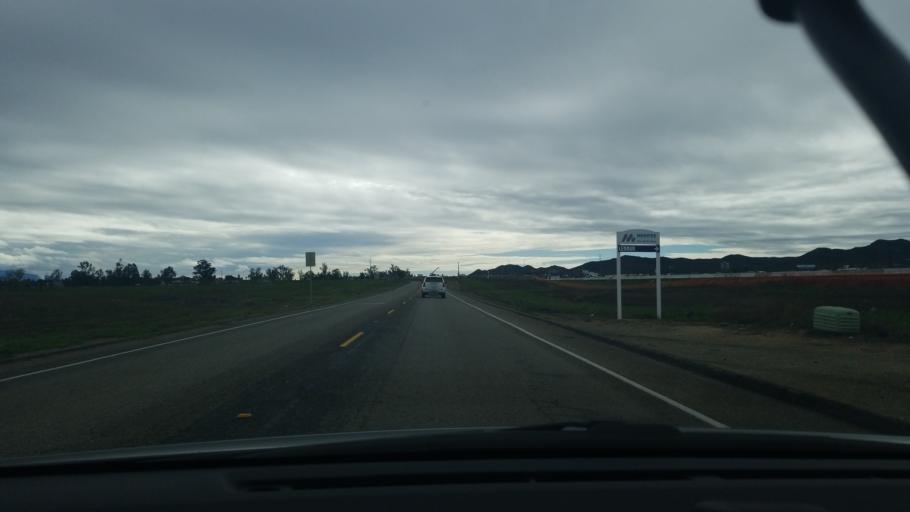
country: US
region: California
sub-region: Riverside County
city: Sun City
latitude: 33.6496
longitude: -117.1704
